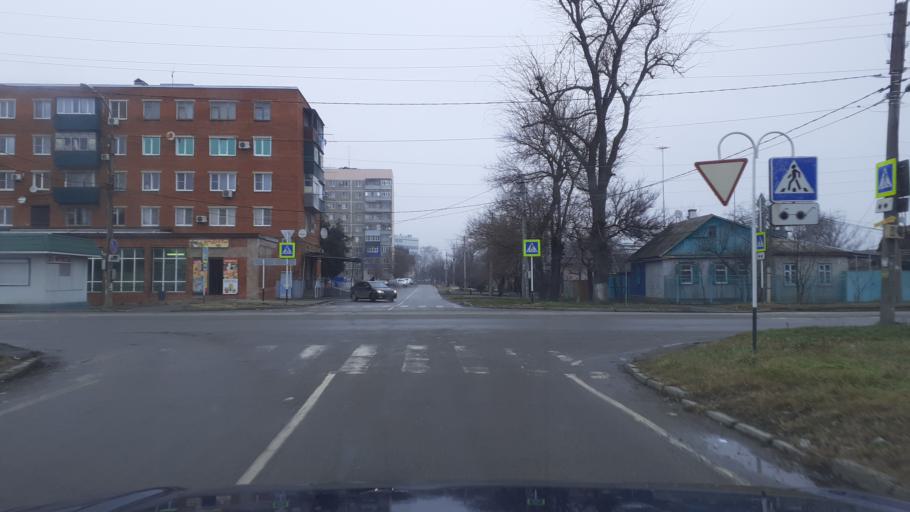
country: RU
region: Adygeya
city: Maykop
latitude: 44.6213
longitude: 40.0700
